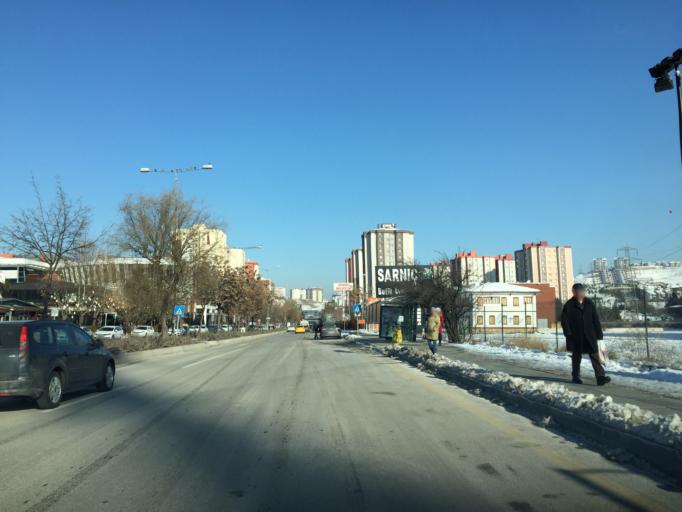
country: TR
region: Ankara
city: Etimesgut
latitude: 39.8814
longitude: 32.6842
